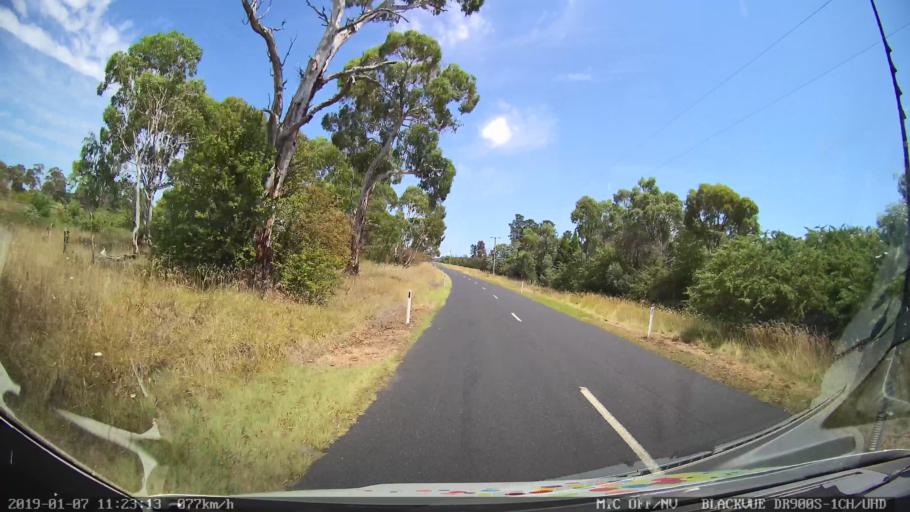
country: AU
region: New South Wales
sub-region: Armidale Dumaresq
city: Armidale
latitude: -30.4767
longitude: 151.6234
